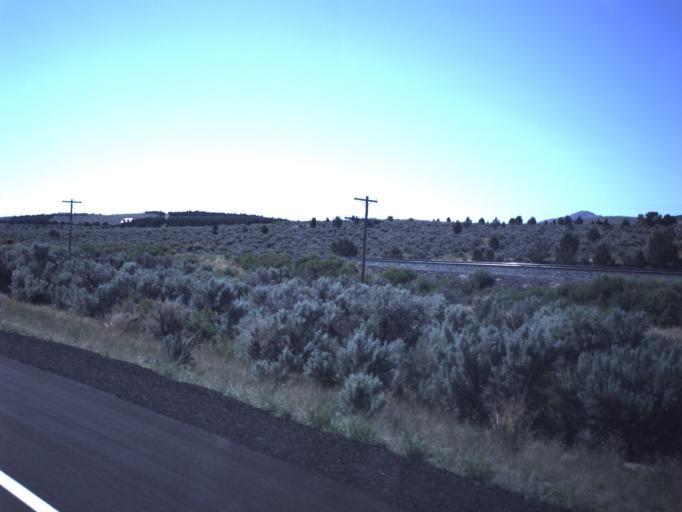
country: US
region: Utah
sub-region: Utah County
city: Genola
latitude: 39.9711
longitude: -112.2567
